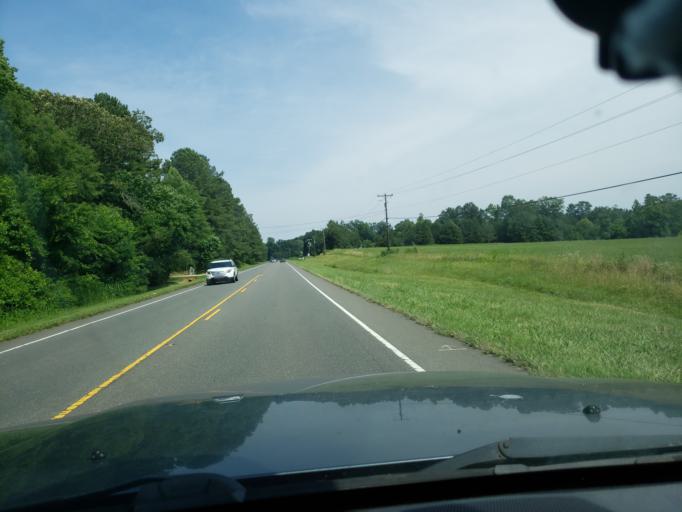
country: US
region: North Carolina
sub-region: Alamance County
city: Saxapahaw
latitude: 35.9351
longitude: -79.2299
